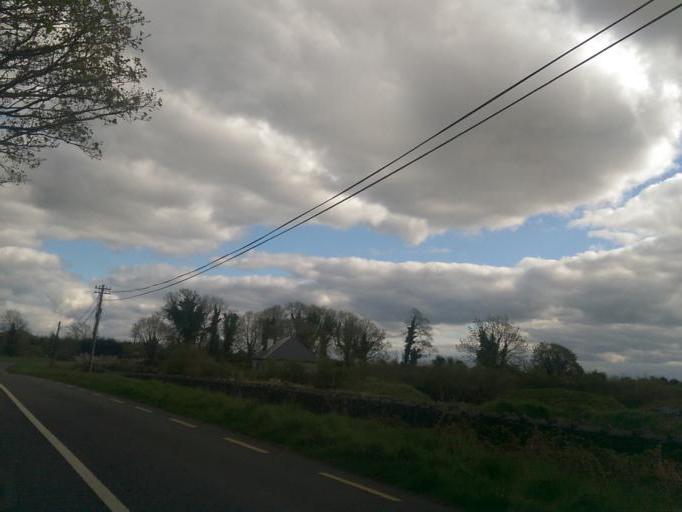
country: IE
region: Connaught
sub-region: County Galway
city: Ballinasloe
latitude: 53.4085
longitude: -8.3376
